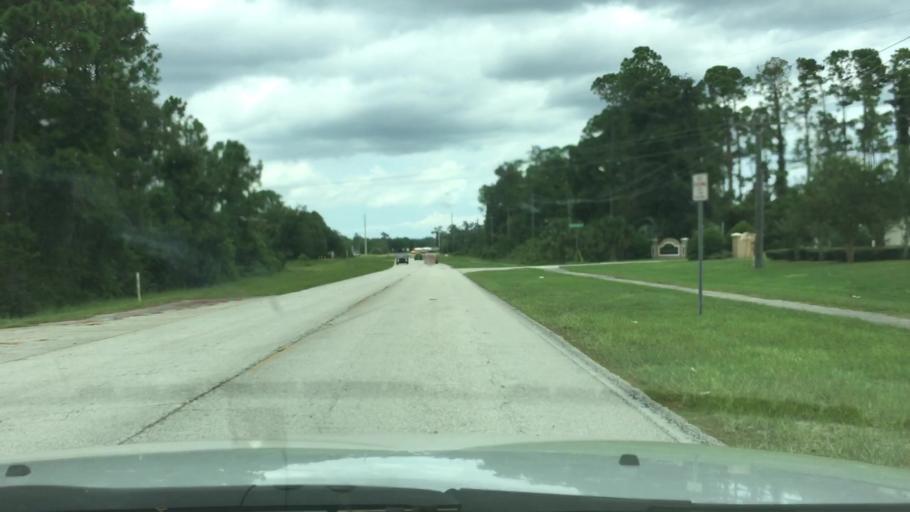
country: US
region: Florida
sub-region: Volusia County
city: Holly Hill
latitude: 29.2294
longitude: -81.0702
